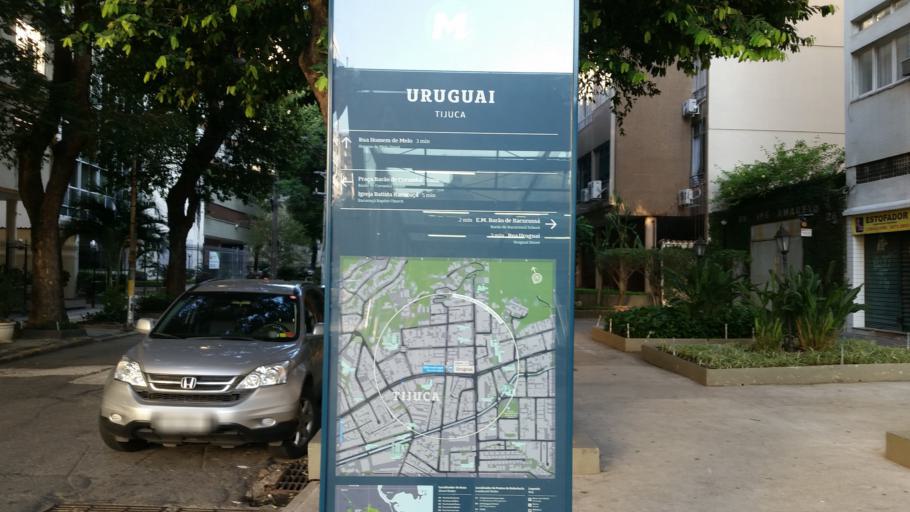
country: BR
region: Rio de Janeiro
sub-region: Rio De Janeiro
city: Rio de Janeiro
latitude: -22.9322
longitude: -43.2392
